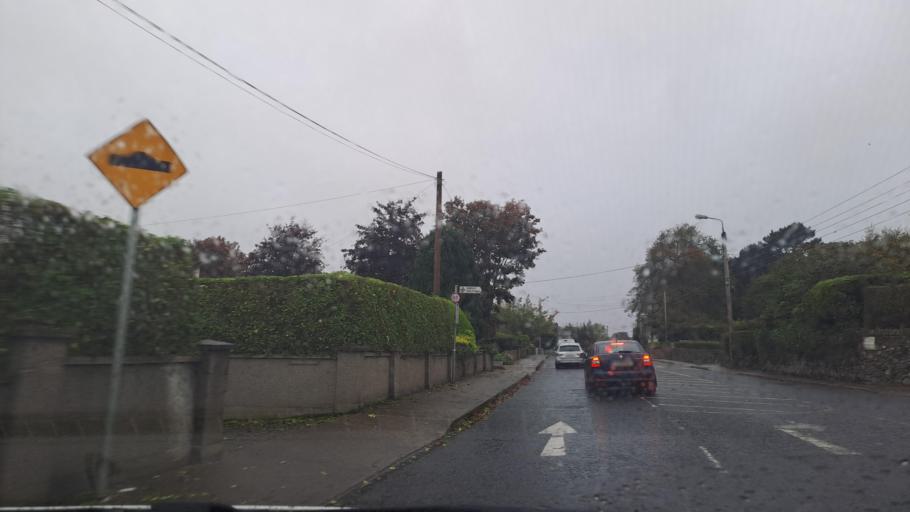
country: IE
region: Leinster
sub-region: Lu
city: Dundalk
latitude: 53.9996
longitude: -6.4225
